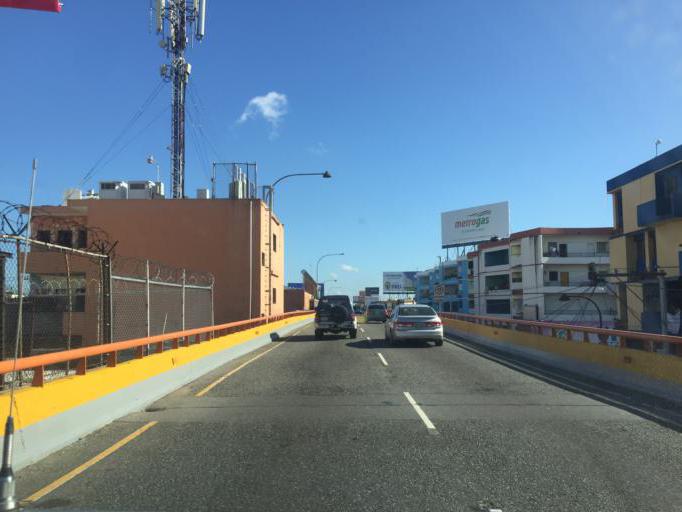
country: DO
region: Nacional
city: San Carlos
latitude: 18.4832
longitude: -69.8923
